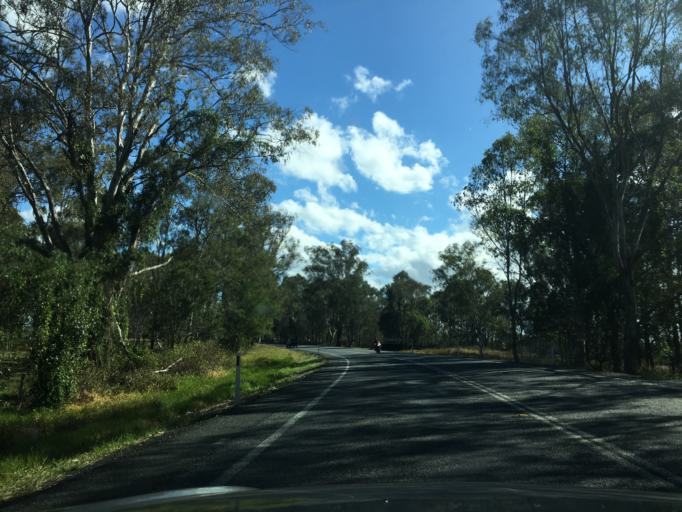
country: AU
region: Queensland
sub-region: Logan
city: Chambers Flat
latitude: -27.7580
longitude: 153.1116
